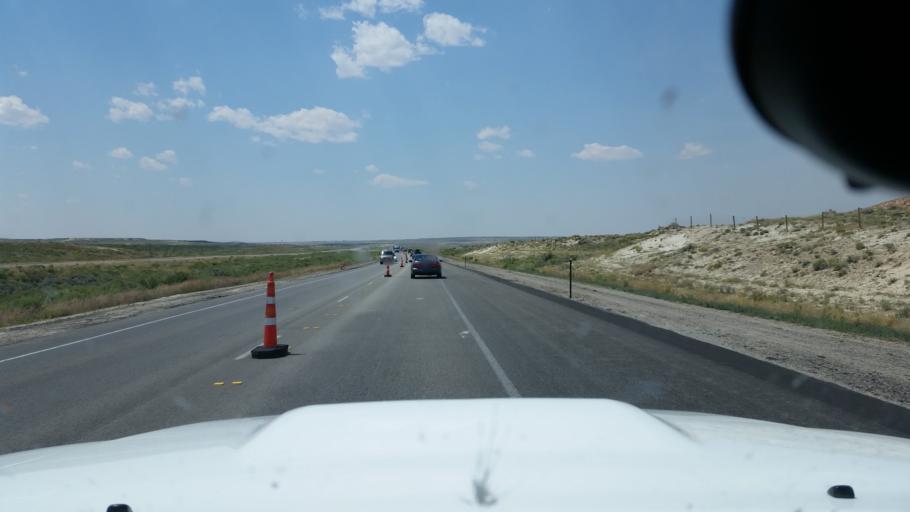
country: US
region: Wyoming
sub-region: Carbon County
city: Rawlins
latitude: 41.7065
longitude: -107.8688
